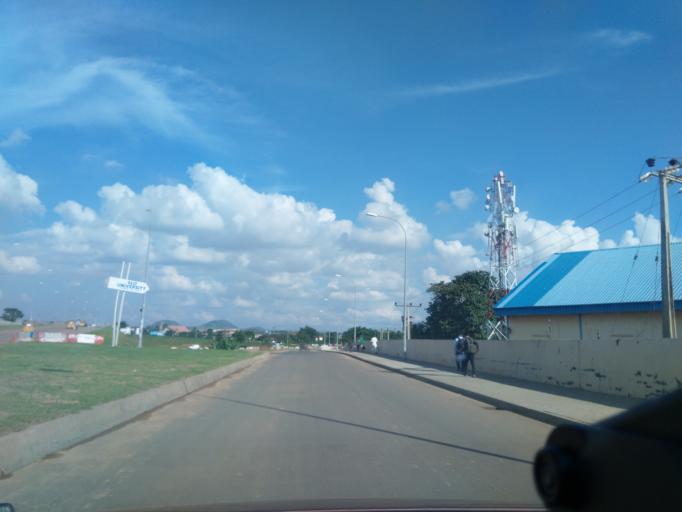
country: NG
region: Abuja Federal Capital Territory
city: Abuja
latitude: 9.0661
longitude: 7.4086
